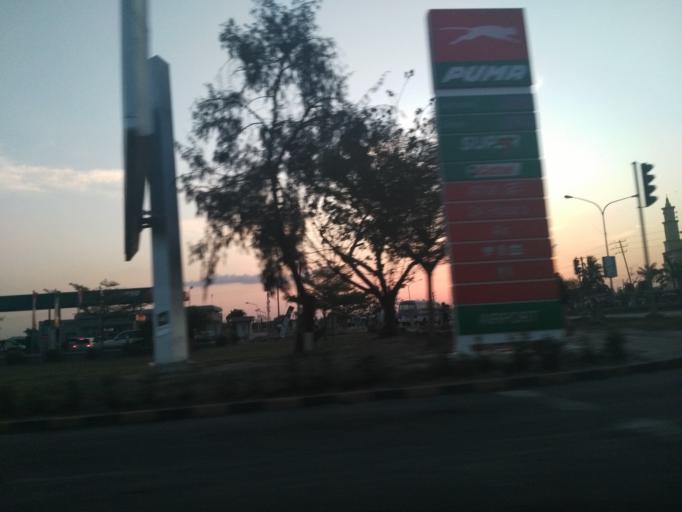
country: TZ
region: Dar es Salaam
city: Dar es Salaam
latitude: -6.8634
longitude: 39.2063
